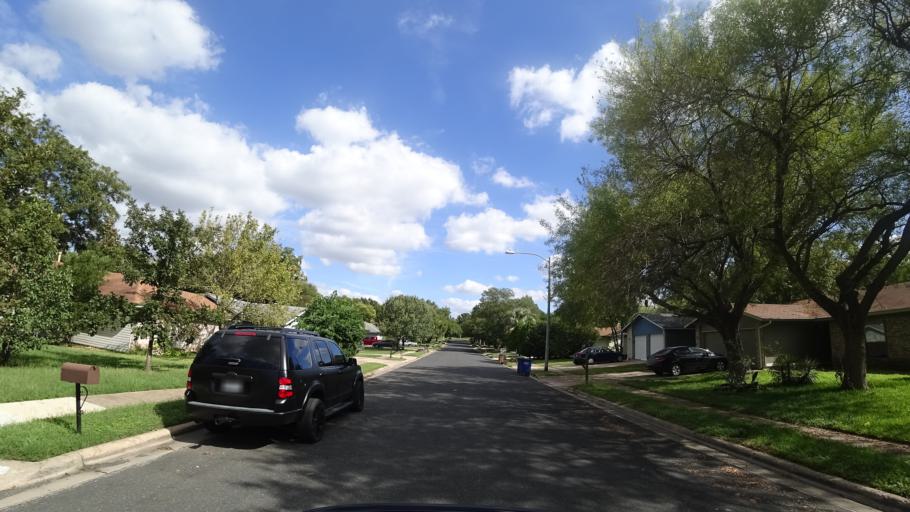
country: US
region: Texas
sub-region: Travis County
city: Onion Creek
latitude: 30.2019
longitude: -97.7948
